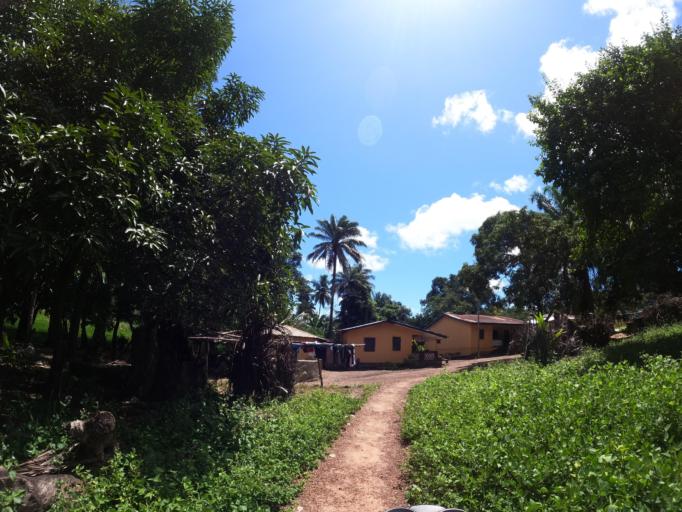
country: SL
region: Northern Province
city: Binkolo
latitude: 9.1087
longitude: -12.2047
